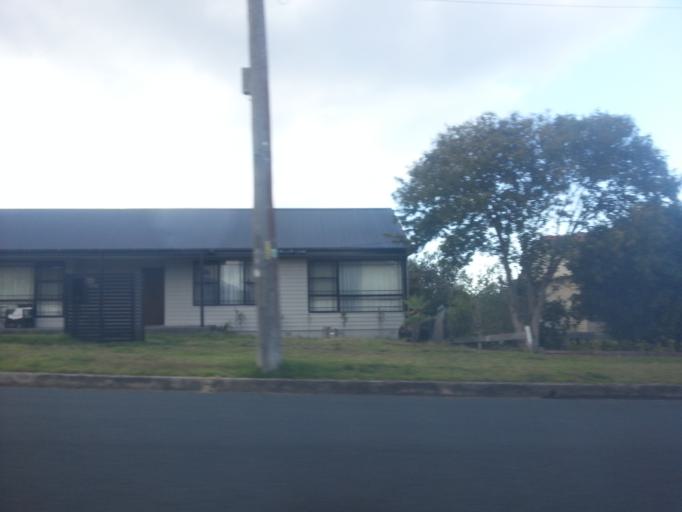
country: AU
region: New South Wales
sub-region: Wollongong
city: West Wollongong
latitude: -34.4223
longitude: 150.8624
